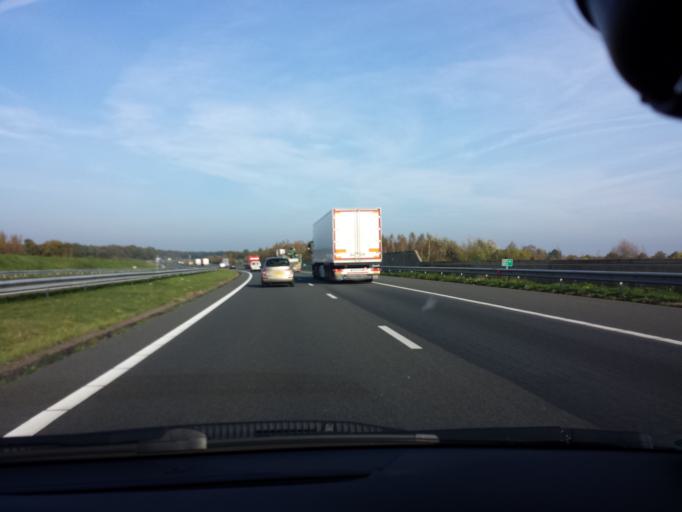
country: NL
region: Limburg
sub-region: Gemeente Beesel
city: Offenbeek
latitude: 51.2800
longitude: 6.1017
